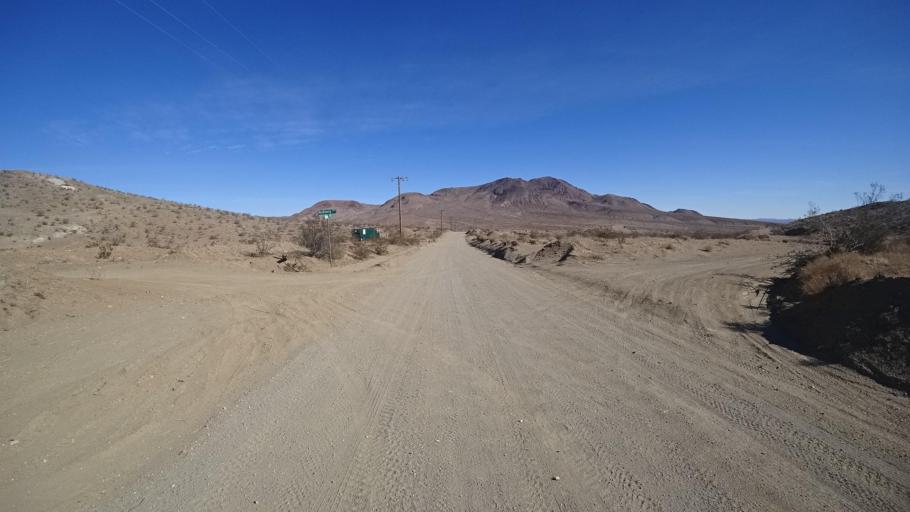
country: US
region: California
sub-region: Kern County
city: Ridgecrest
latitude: 35.3444
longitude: -117.6307
